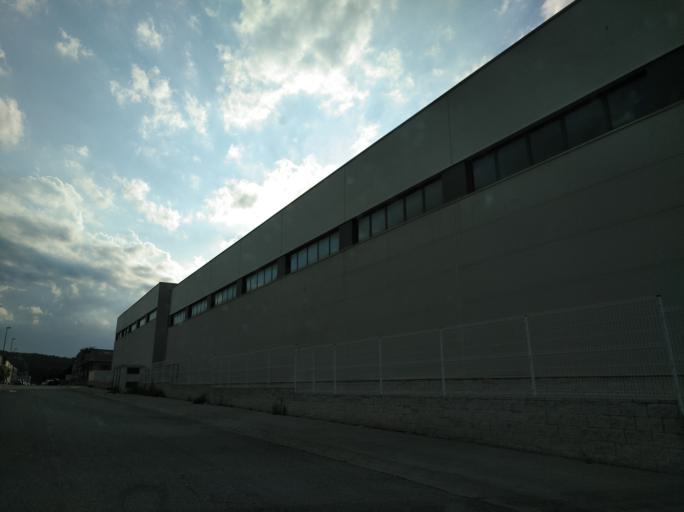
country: ES
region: Catalonia
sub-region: Provincia de Girona
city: Vilablareix
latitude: 41.9688
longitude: 2.7778
